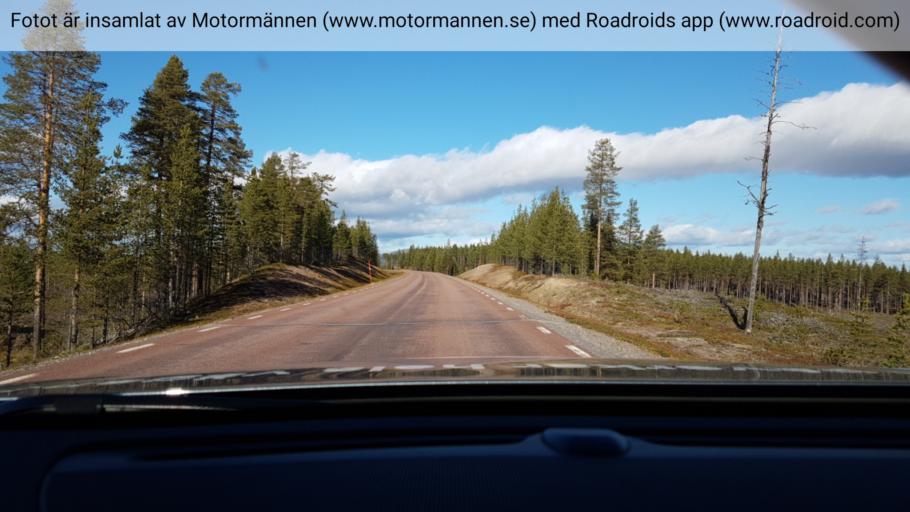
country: SE
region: Norrbotten
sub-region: Arjeplogs Kommun
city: Arjeplog
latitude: 66.0310
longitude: 18.0593
